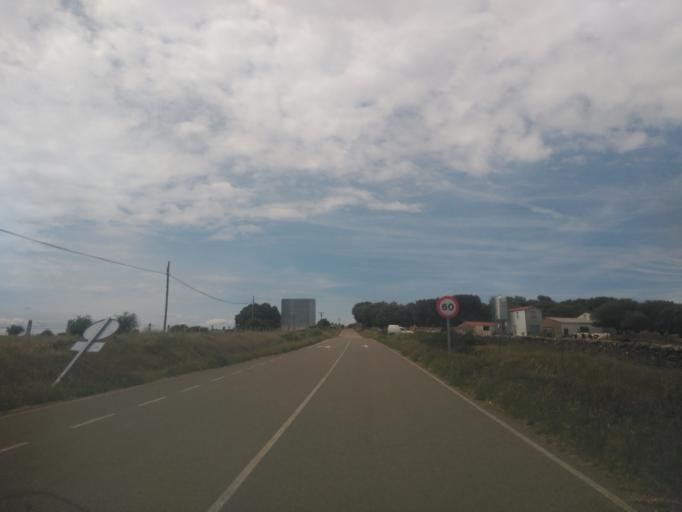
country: ES
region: Castille and Leon
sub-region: Provincia de Salamanca
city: Guijuelo
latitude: 40.5420
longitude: -5.6624
